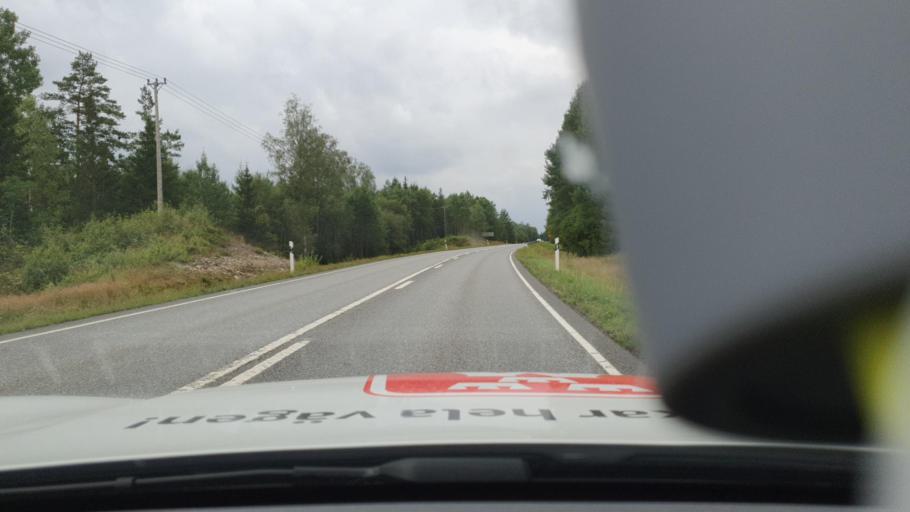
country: SE
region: Joenkoeping
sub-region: Gislaveds Kommun
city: Smalandsstenar
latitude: 57.1854
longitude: 13.4337
